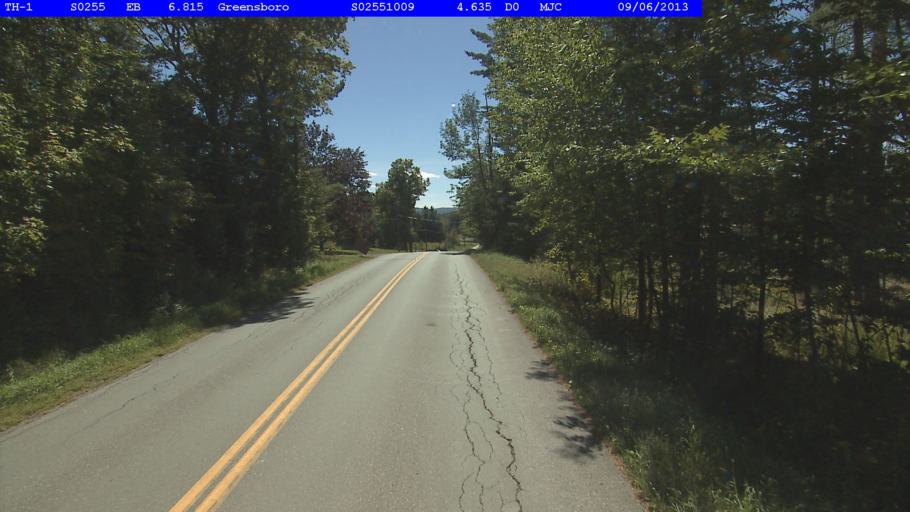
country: US
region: Vermont
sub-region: Caledonia County
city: Hardwick
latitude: 44.5820
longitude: -72.2967
